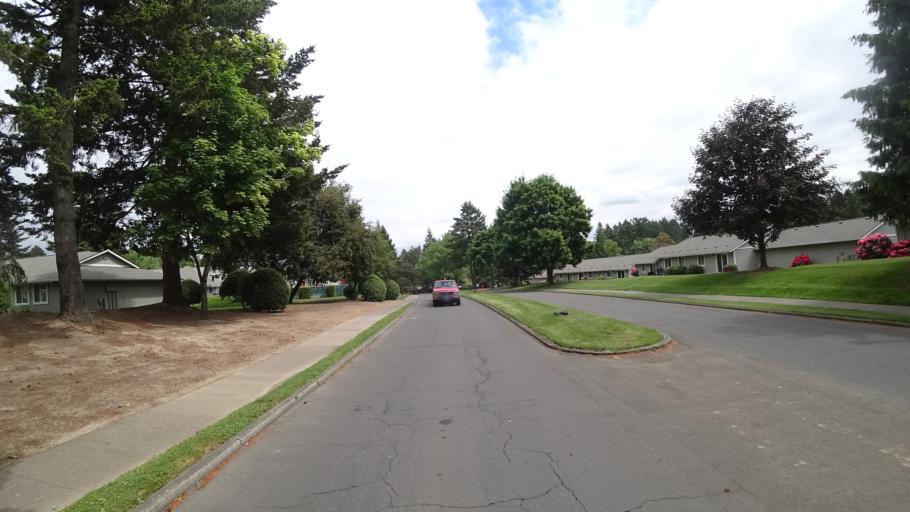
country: US
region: Oregon
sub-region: Washington County
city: Aloha
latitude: 45.5205
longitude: -122.8654
